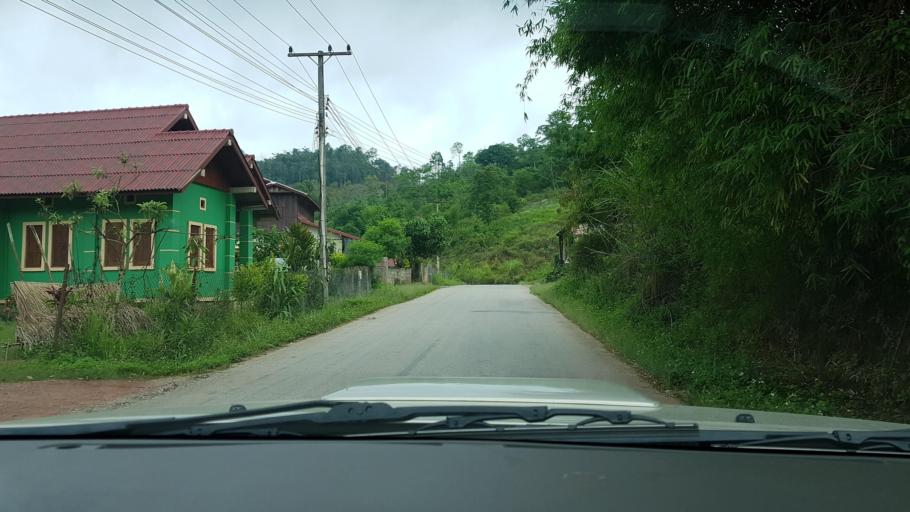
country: LA
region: Oudomxai
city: Muang Xay
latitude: 20.5869
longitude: 101.9300
